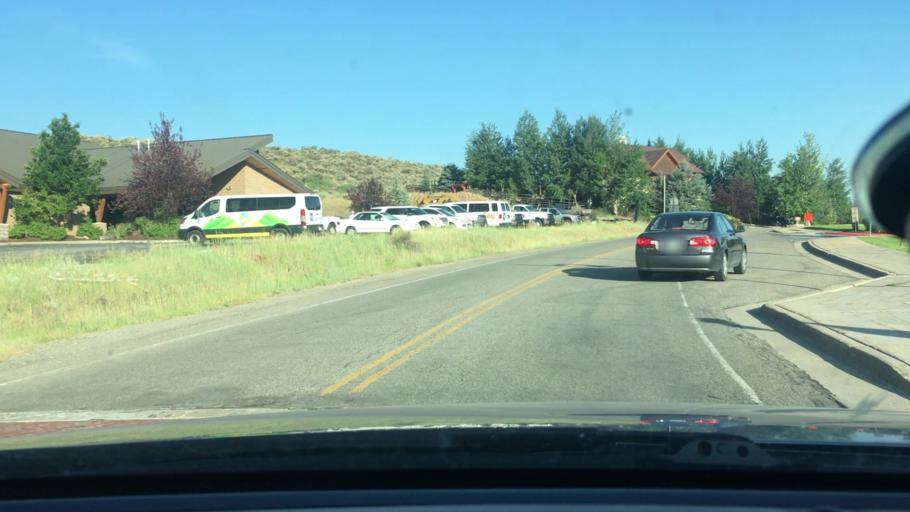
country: US
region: Utah
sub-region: Summit County
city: Snyderville
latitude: 40.7145
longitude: -111.5032
